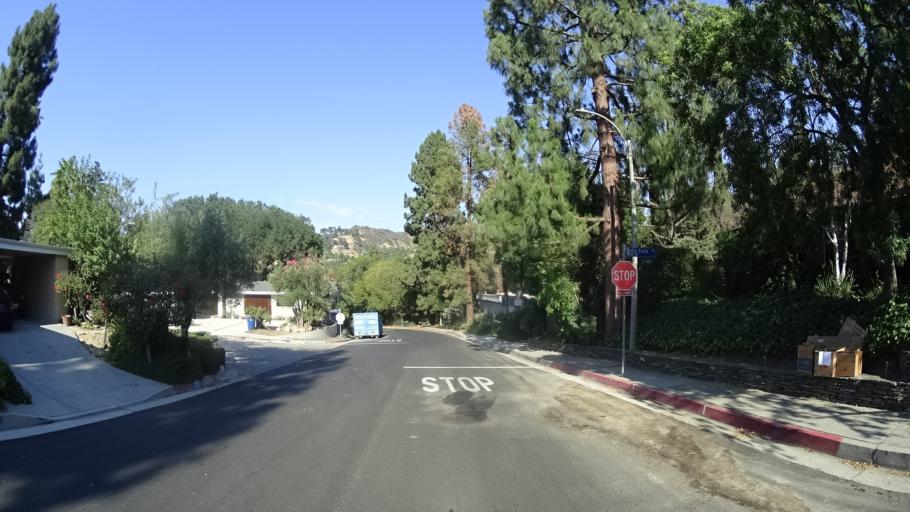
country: US
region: California
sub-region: Los Angeles County
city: Universal City
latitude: 34.1271
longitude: -118.3814
